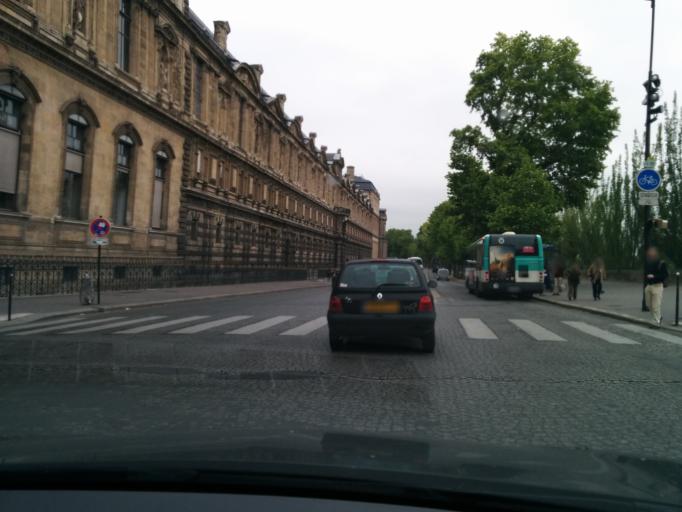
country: FR
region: Ile-de-France
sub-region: Paris
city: Paris
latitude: 48.8601
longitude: 2.3336
